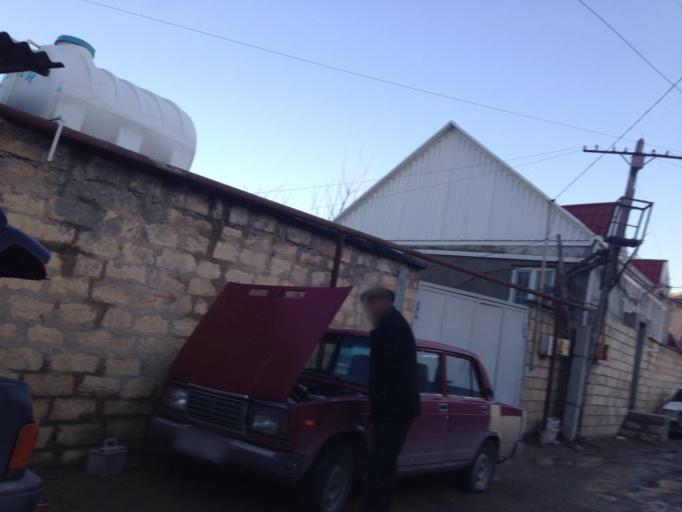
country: AZ
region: Baki
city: Baku
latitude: 40.4155
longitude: 49.8659
